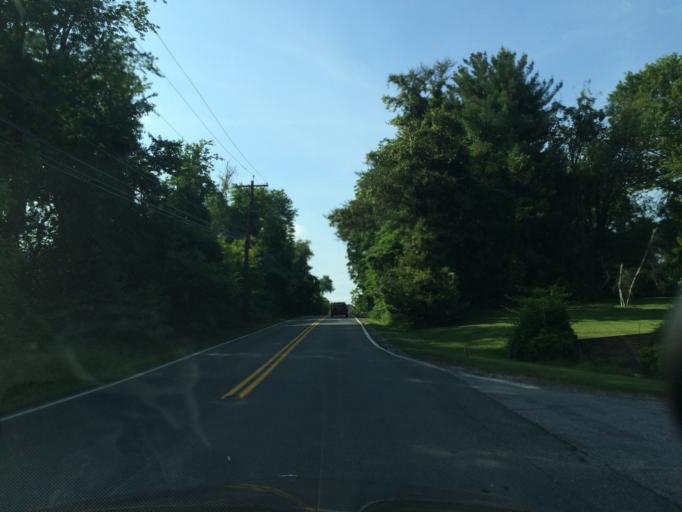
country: US
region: Maryland
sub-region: Montgomery County
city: Olney
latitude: 39.1868
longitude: -77.0642
